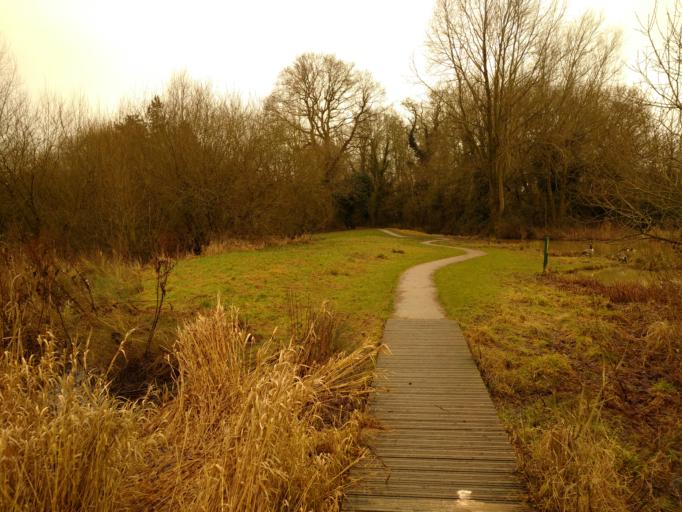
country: GB
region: England
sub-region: Milton Keynes
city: Milton Keynes
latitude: 52.0124
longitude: -0.7606
